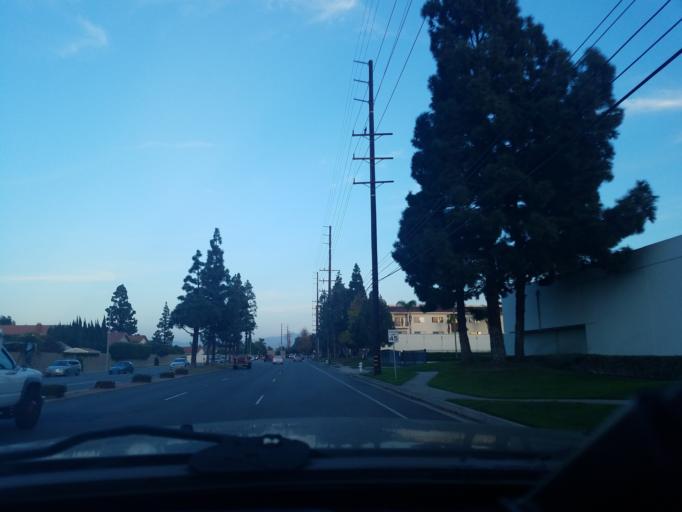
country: US
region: California
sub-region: Orange County
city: Fountain Valley
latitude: 33.7163
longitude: -117.9281
